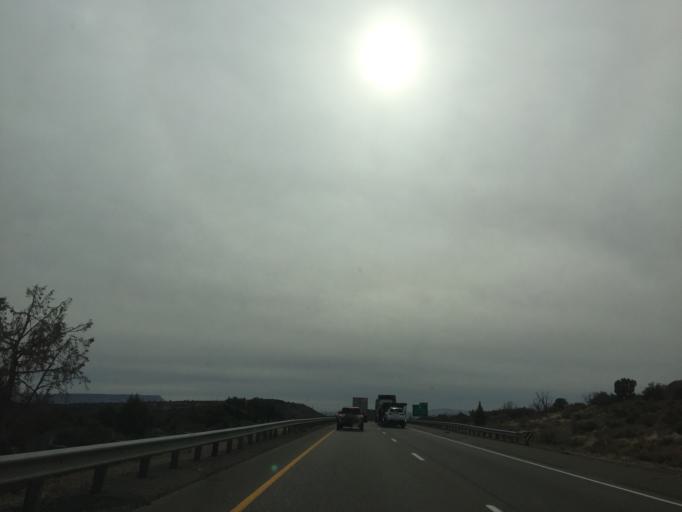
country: US
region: Utah
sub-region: Washington County
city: Toquerville
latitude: 37.2960
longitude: -113.2999
